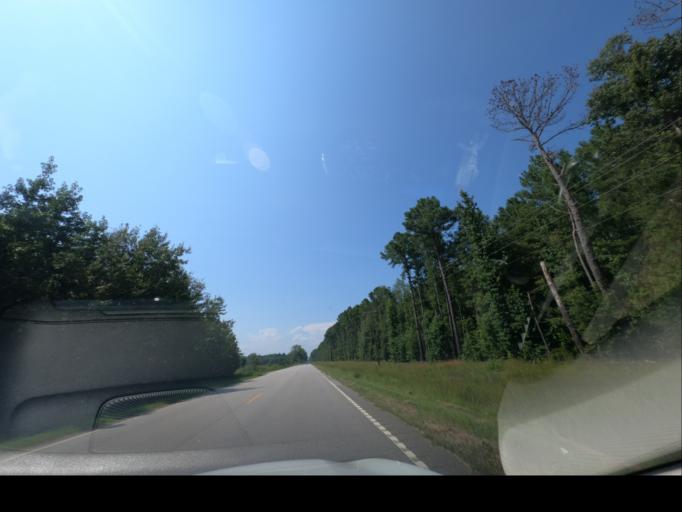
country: US
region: South Carolina
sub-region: Richland County
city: Hopkins
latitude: 33.8787
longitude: -80.9022
